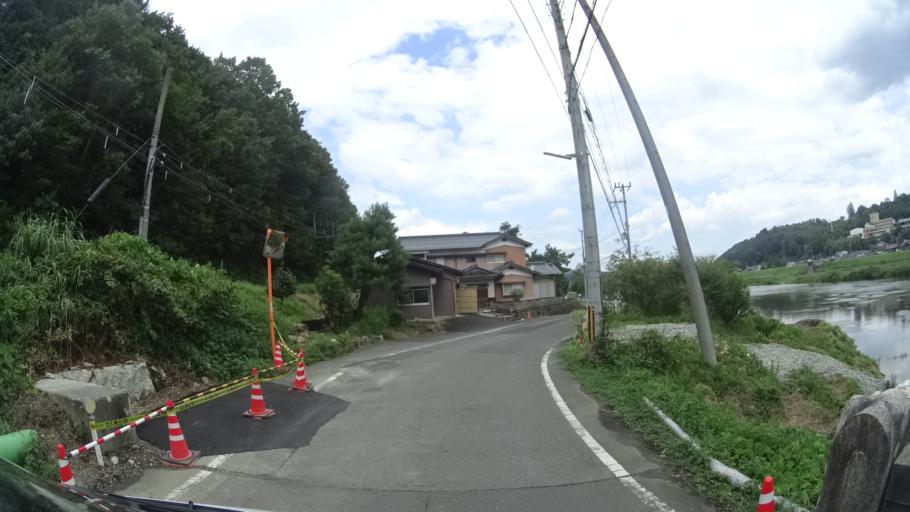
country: JP
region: Kyoto
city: Ayabe
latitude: 35.2930
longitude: 135.2636
